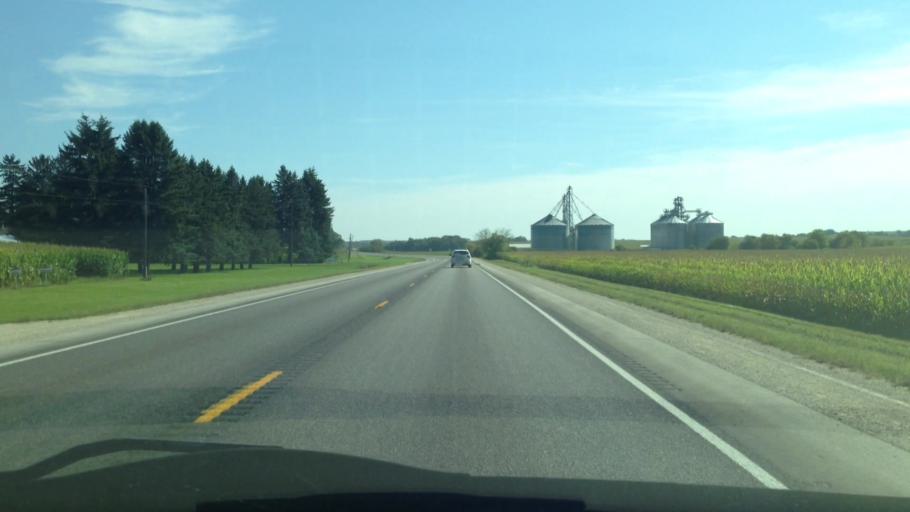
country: US
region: Minnesota
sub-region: Houston County
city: Spring Grove
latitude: 43.5149
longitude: -91.7999
